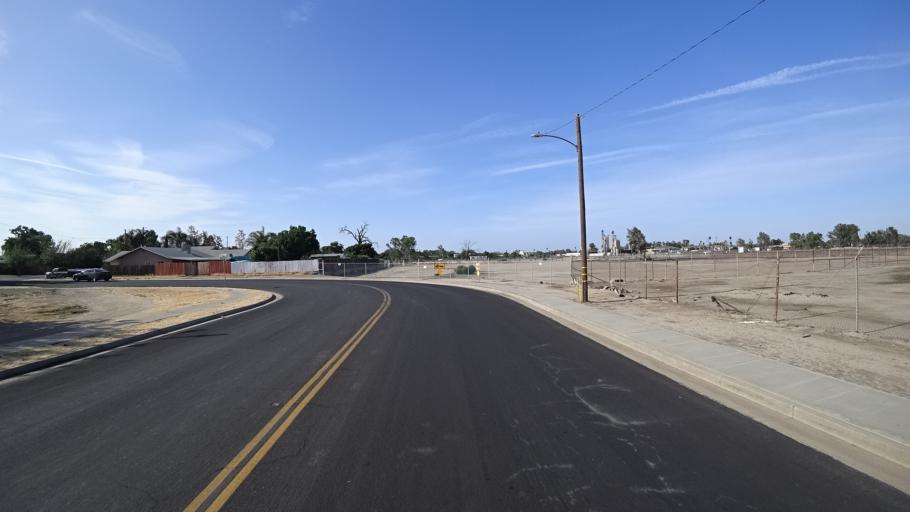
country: US
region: California
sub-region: Kings County
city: Hanford
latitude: 36.3202
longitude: -119.6493
